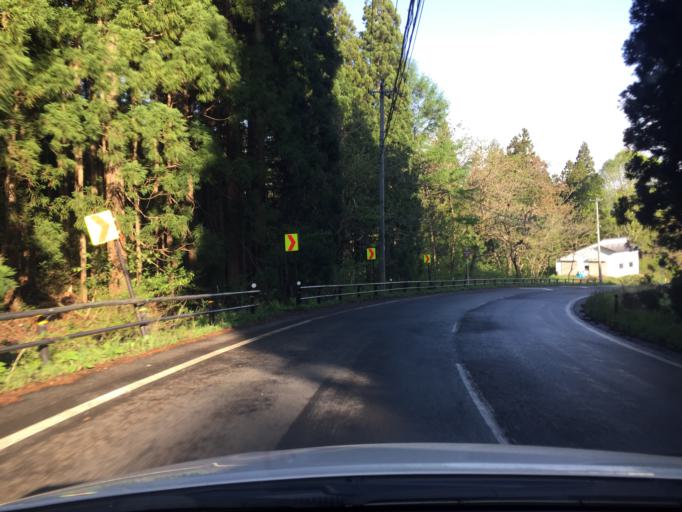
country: JP
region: Fukushima
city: Kitakata
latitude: 37.6610
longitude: 139.9914
